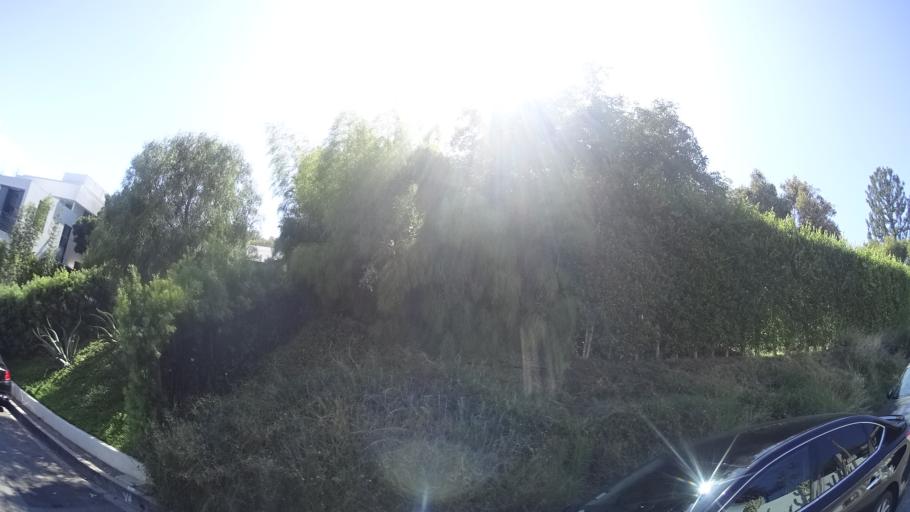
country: US
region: California
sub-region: Los Angeles County
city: West Hollywood
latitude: 34.0940
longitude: -118.3788
